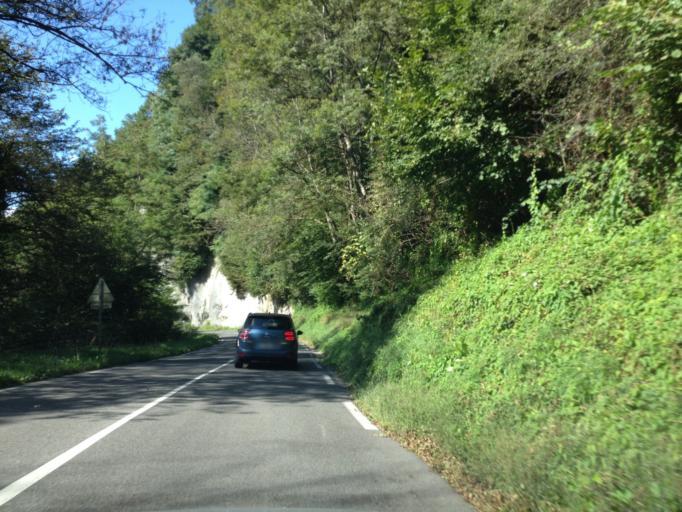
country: FR
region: Rhone-Alpes
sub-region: Departement de la Savoie
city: Gresy-sur-Aix
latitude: 45.7295
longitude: 5.9499
